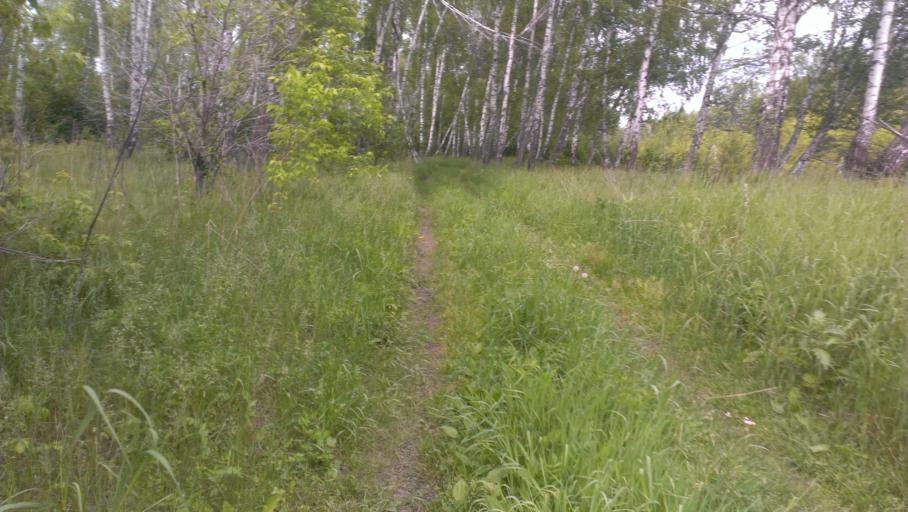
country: RU
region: Altai Krai
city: Sannikovo
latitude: 53.3407
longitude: 84.0580
